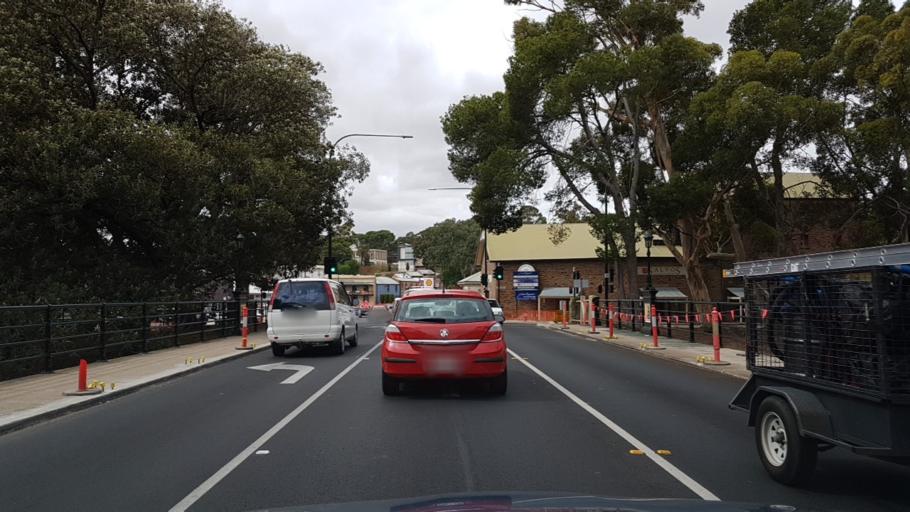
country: AU
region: South Australia
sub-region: Gawler
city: Gawler
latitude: -34.6037
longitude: 138.7470
